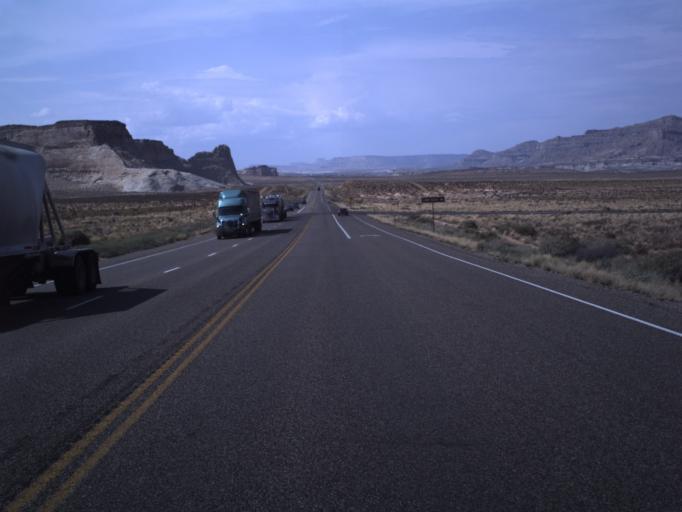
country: US
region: Arizona
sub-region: Coconino County
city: Page
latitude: 37.0052
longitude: -111.5767
